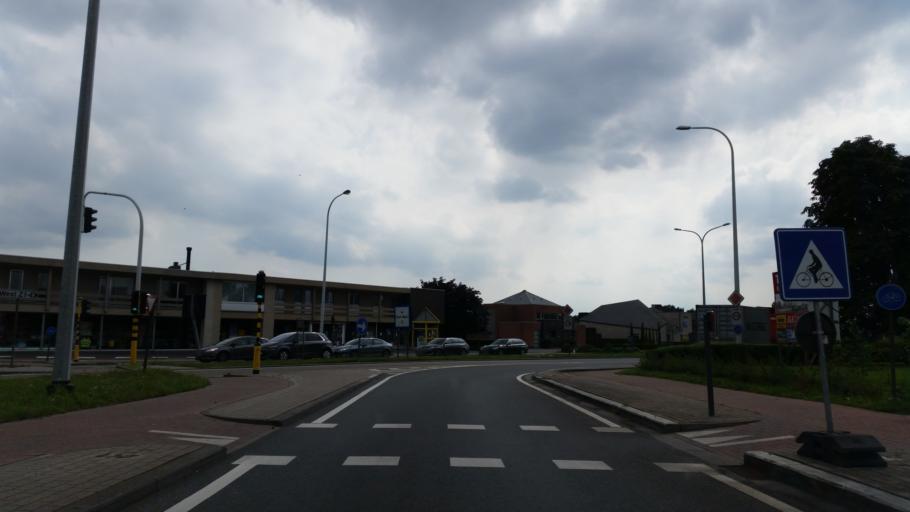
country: BE
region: Flanders
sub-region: Provincie Antwerpen
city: Geel
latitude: 51.1529
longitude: 4.9745
